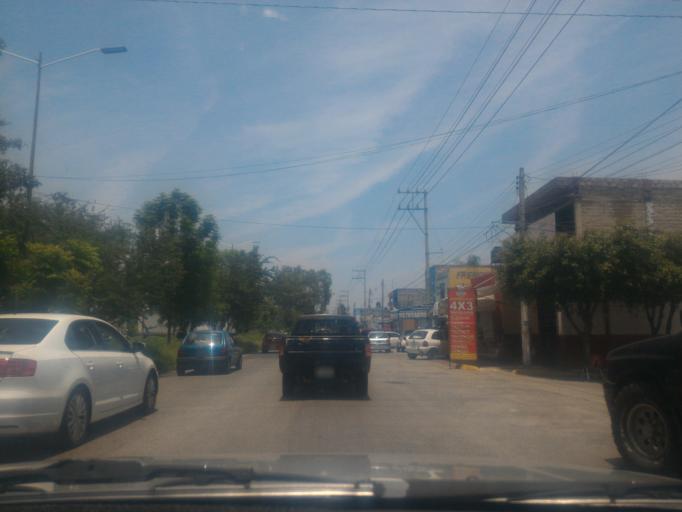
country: MX
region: Jalisco
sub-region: Tlajomulco de Zuniga
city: Altus Bosques
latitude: 20.6203
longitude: -103.3549
